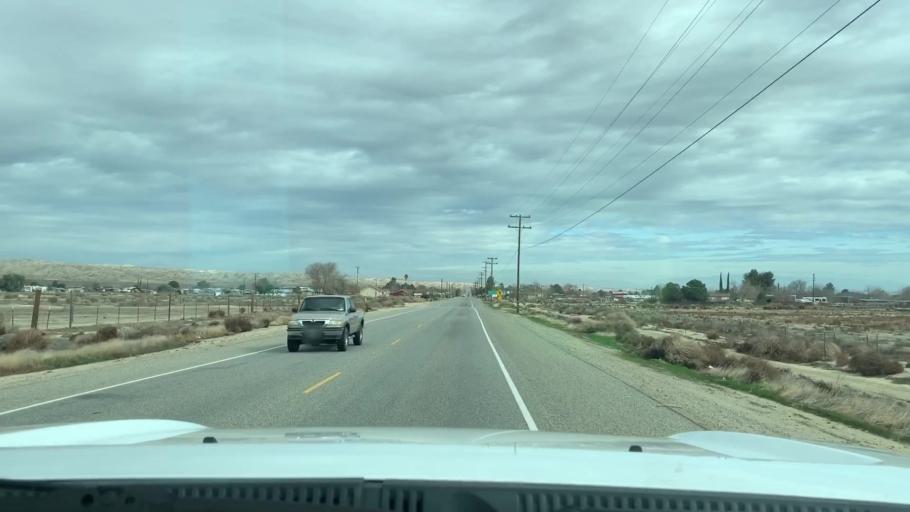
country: US
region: California
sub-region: Kern County
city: Ford City
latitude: 35.2156
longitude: -119.3962
